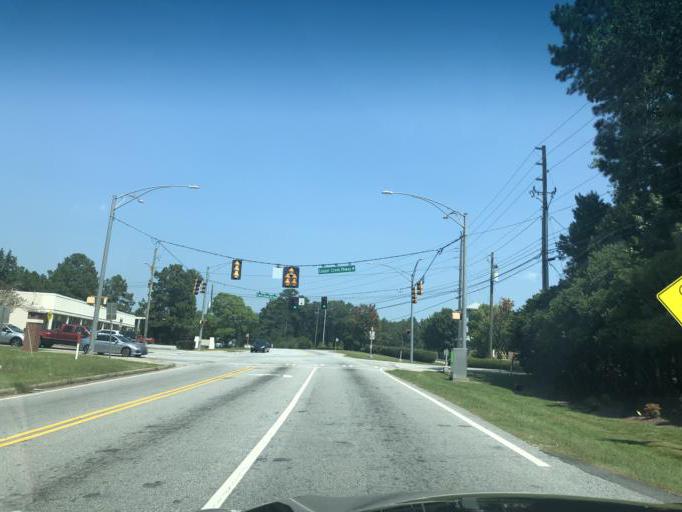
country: US
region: Georgia
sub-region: Muscogee County
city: Columbus
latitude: 32.5148
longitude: -84.9131
